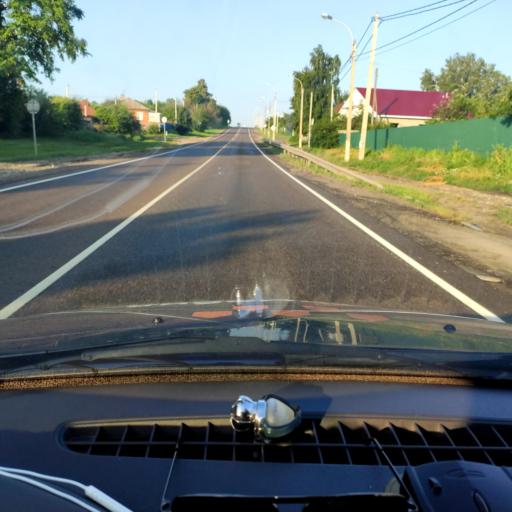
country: RU
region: Lipetsk
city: Kazaki
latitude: 52.6228
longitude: 38.2713
